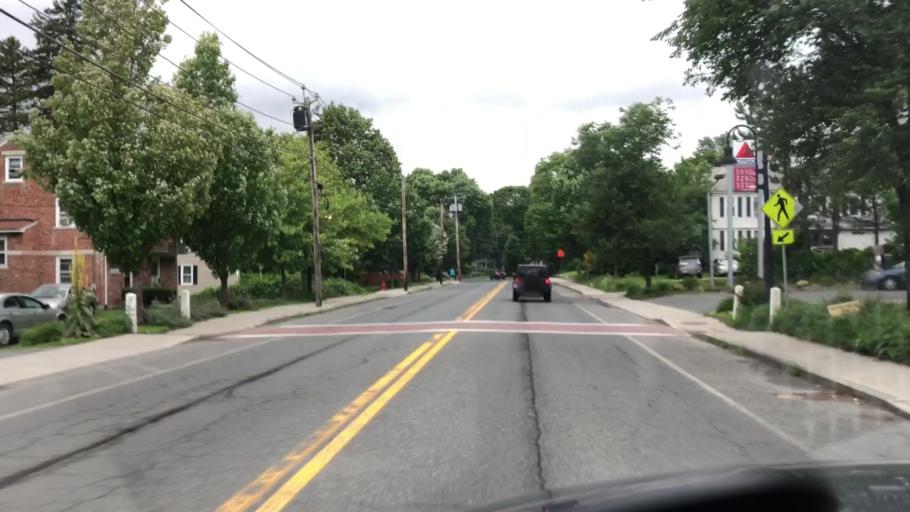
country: US
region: Massachusetts
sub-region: Berkshire County
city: Lee
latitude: 42.3031
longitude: -73.2448
